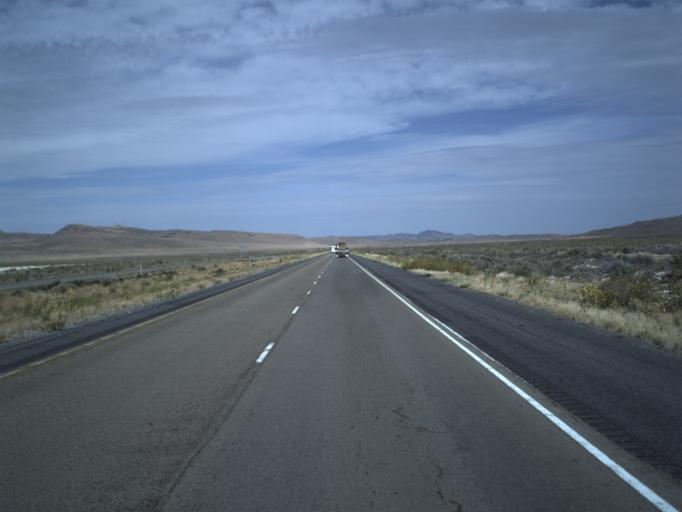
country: US
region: Utah
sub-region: Tooele County
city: Grantsville
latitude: 40.7716
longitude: -112.7972
